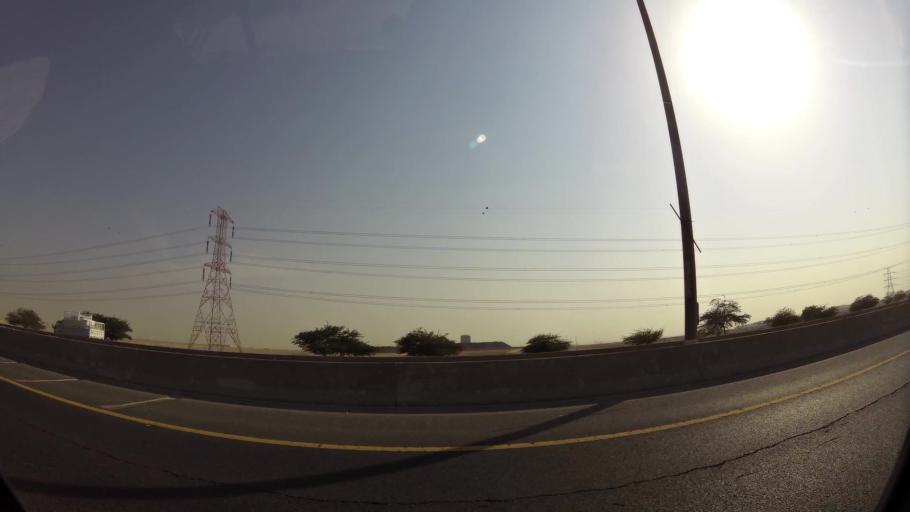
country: KW
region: Al Ahmadi
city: Al Ahmadi
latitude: 29.0168
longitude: 48.0923
